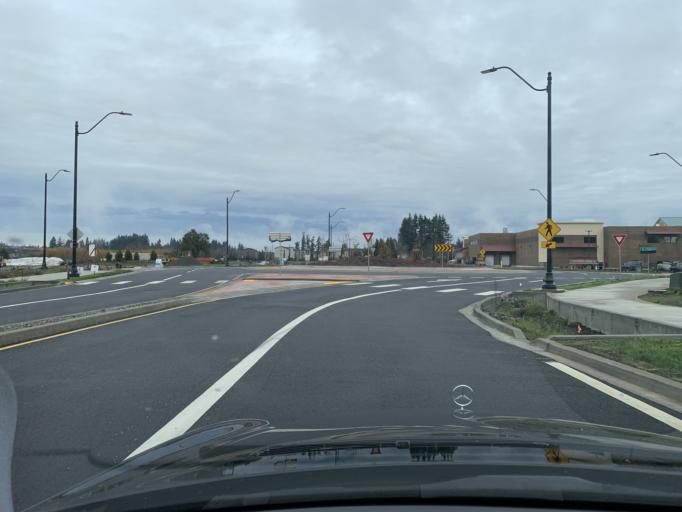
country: US
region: Washington
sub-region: Clark County
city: Ridgefield
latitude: 45.8133
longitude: -122.7028
